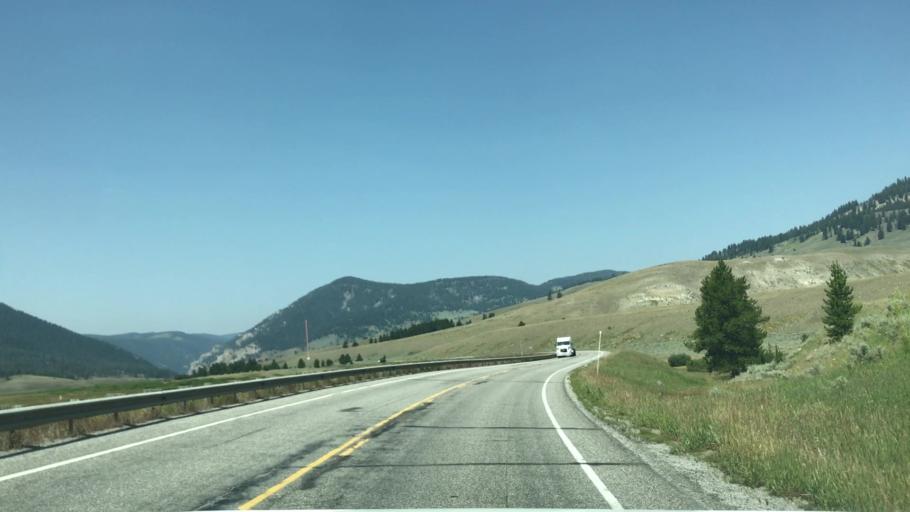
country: US
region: Montana
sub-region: Gallatin County
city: Big Sky
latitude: 45.0434
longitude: -111.1312
